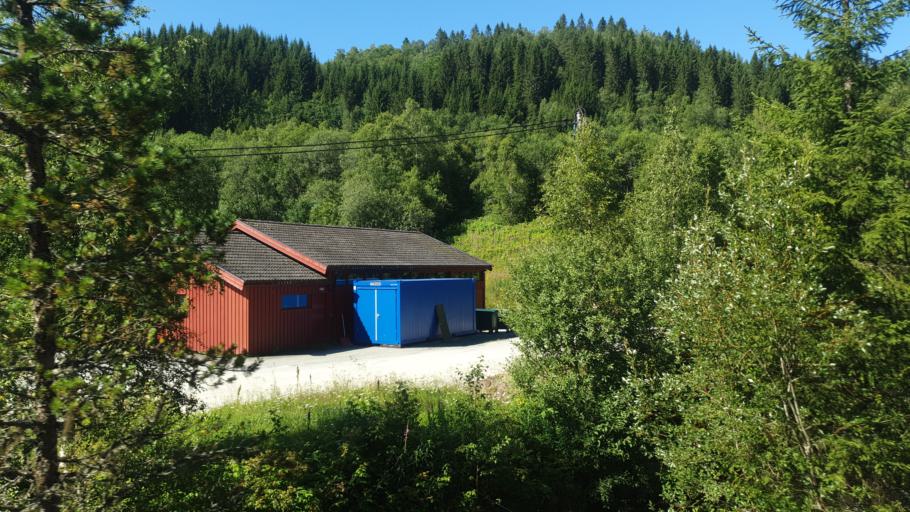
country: NO
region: Sor-Trondelag
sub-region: Meldal
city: Meldal
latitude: 63.1331
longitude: 9.7094
